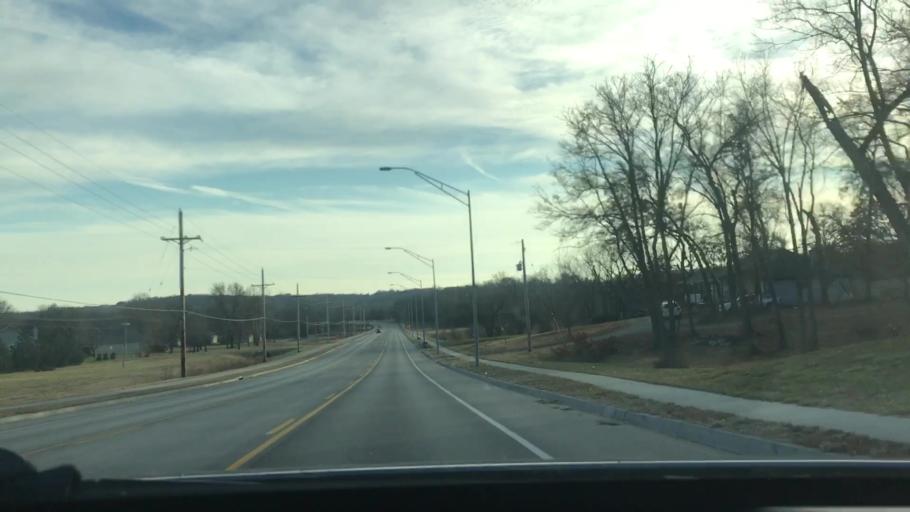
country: US
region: Missouri
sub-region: Jackson County
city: Independence
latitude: 39.0260
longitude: -94.3883
